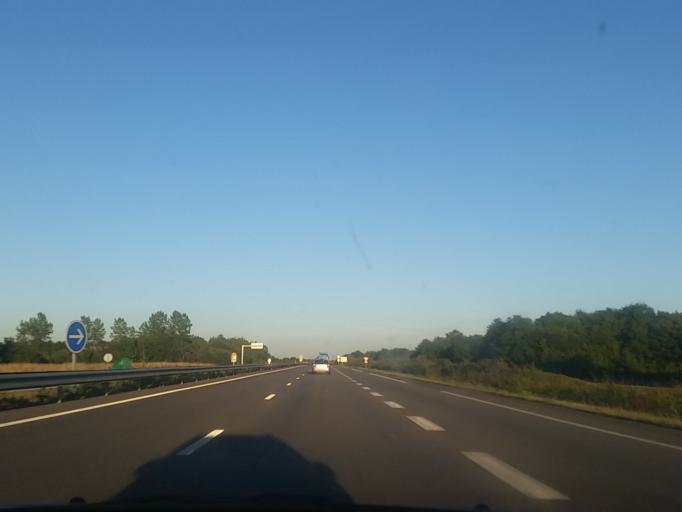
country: FR
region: Pays de la Loire
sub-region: Departement de la Loire-Atlantique
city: Saint-Jean-de-Boiseau
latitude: 47.1828
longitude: -1.7219
